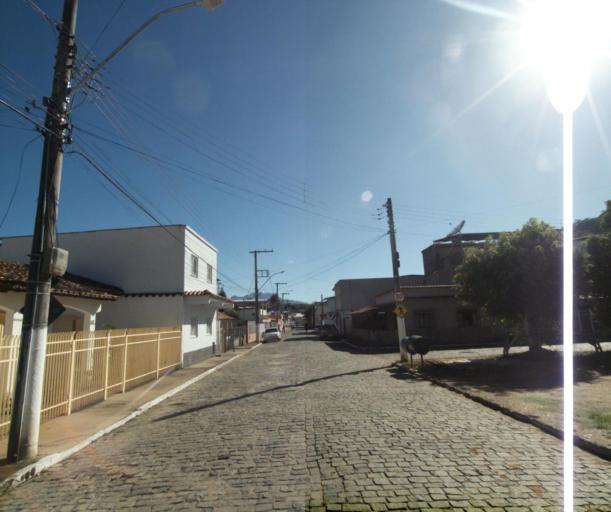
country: BR
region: Minas Gerais
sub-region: Espera Feliz
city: Espera Feliz
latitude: -20.6906
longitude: -41.8495
